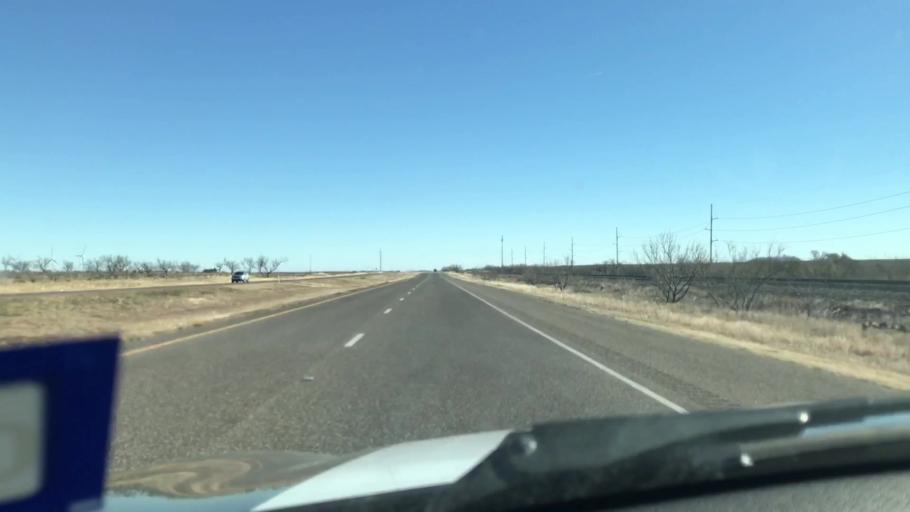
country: US
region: Texas
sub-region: Scurry County
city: Snyder
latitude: 32.8708
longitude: -101.0389
